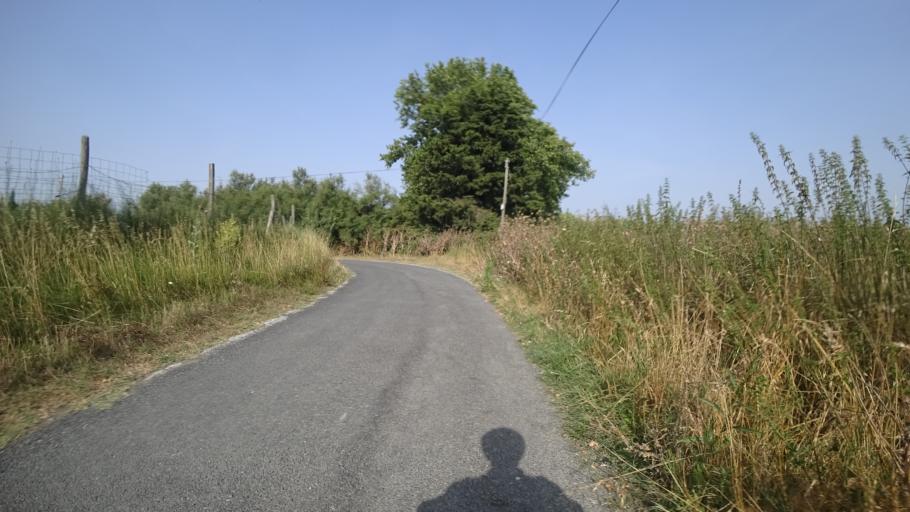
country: FR
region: Languedoc-Roussillon
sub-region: Departement des Pyrenees-Orientales
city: Villelongue-de-la-Salanque
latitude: 42.7351
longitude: 2.9923
